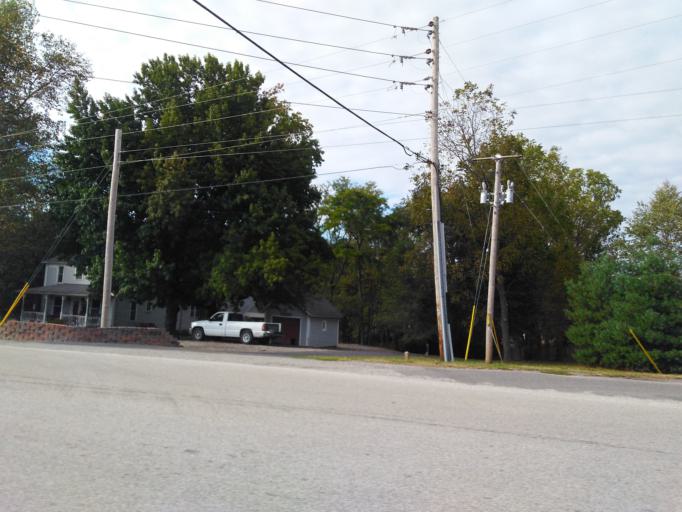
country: US
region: Illinois
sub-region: Bond County
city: Greenville
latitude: 38.9018
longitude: -89.4007
